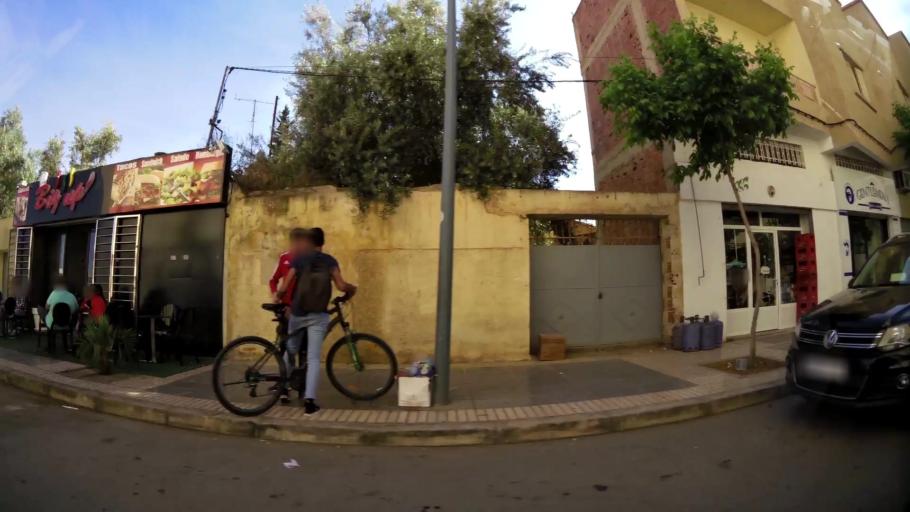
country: MA
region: Oriental
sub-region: Oujda-Angad
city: Oujda
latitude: 34.6719
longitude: -1.9126
